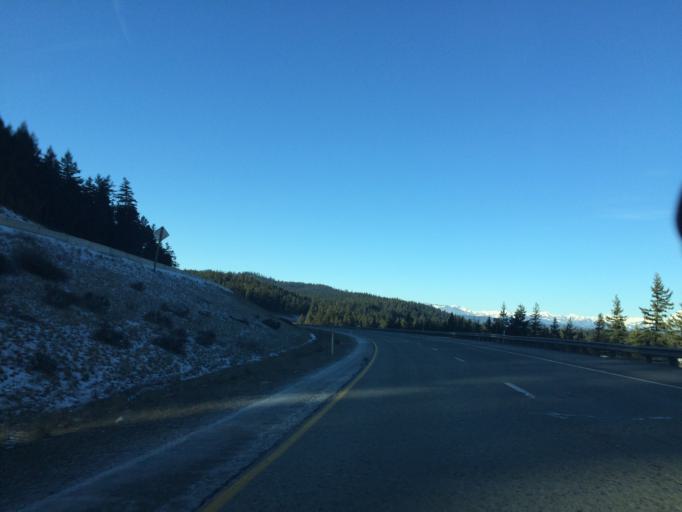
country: US
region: Washington
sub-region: Kittitas County
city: Cle Elum
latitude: 47.1284
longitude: -120.8039
